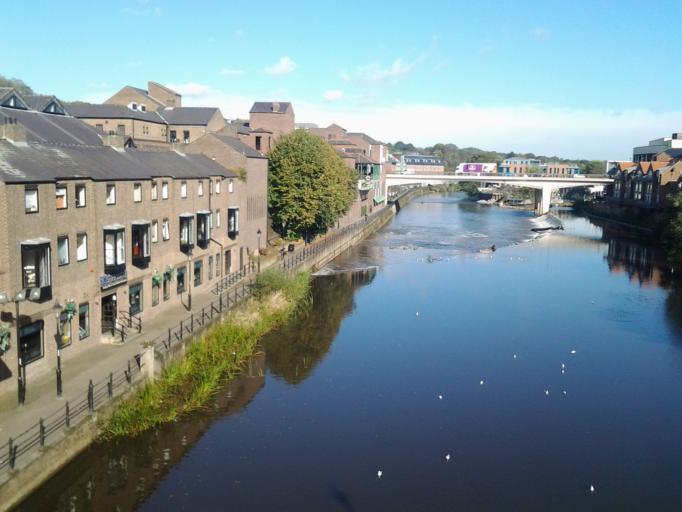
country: GB
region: England
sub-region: County Durham
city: Durham
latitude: 54.7761
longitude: -1.5782
